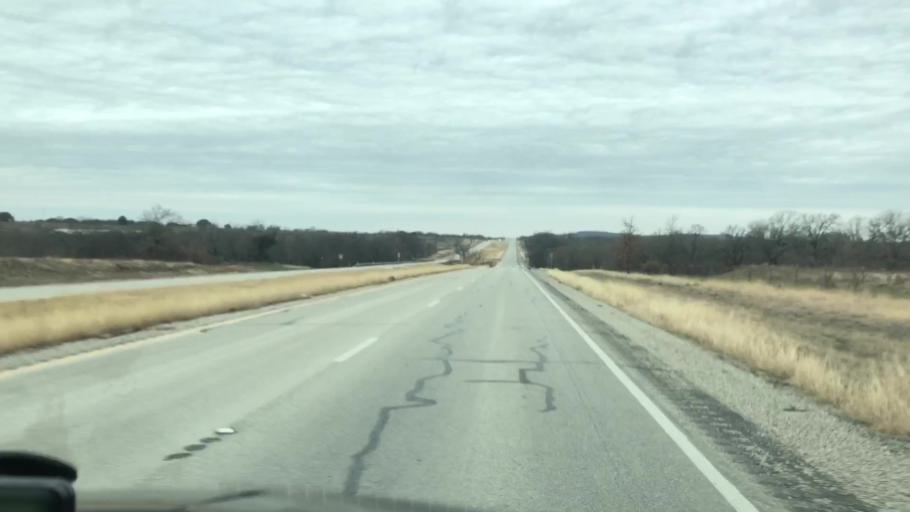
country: US
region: Texas
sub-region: Jack County
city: Jacksboro
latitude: 33.2393
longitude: -98.2148
